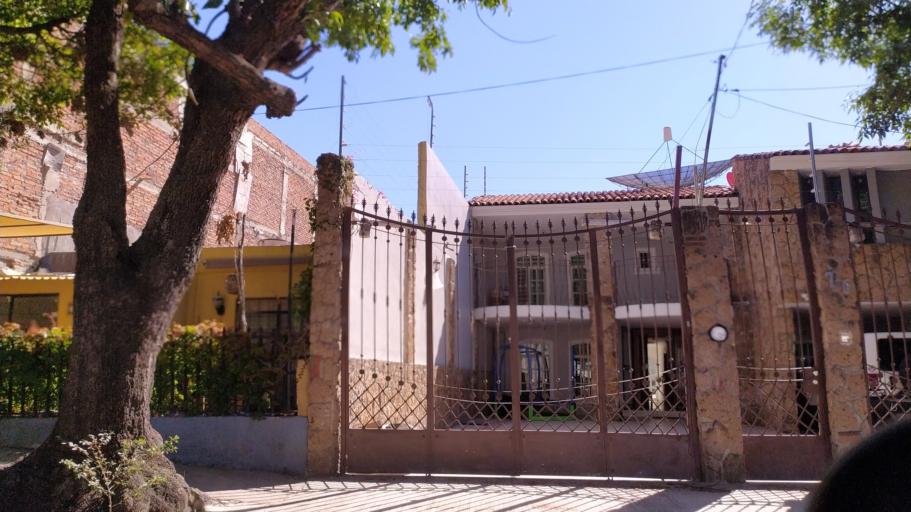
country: MX
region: Jalisco
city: Guadalajara
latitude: 20.6766
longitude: -103.4501
